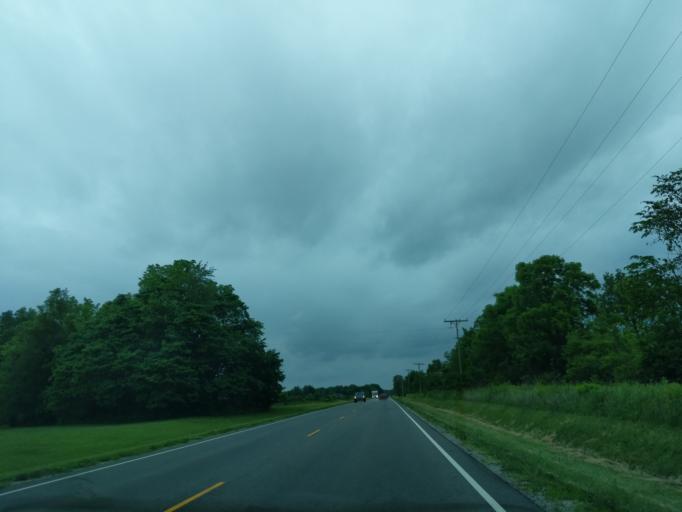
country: US
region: Indiana
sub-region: Madison County
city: Chesterfield
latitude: 40.1019
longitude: -85.6045
